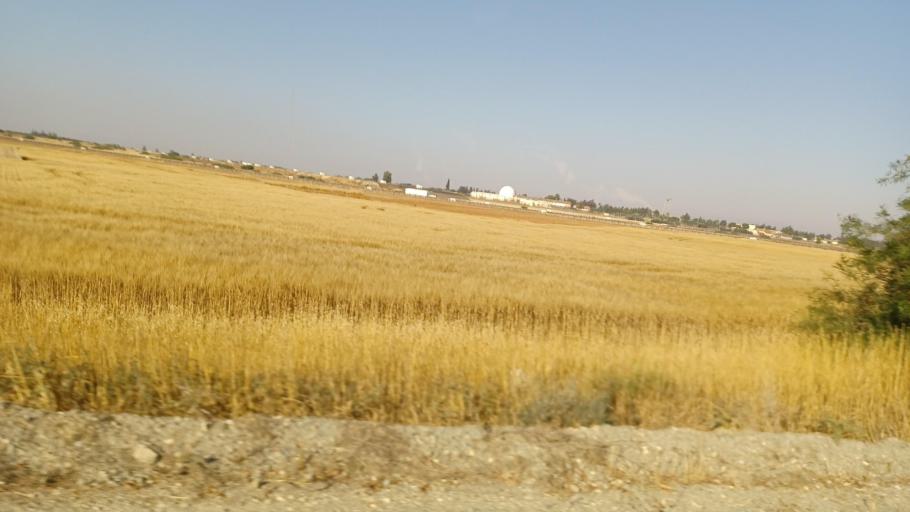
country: CY
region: Ammochostos
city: Acheritou
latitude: 35.0870
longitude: 33.9061
